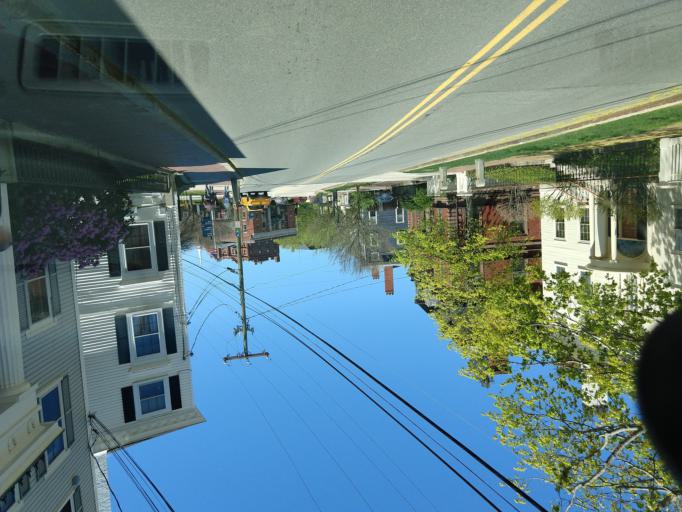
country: US
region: New Hampshire
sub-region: Rockingham County
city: Portsmouth
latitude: 43.0736
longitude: -70.7611
